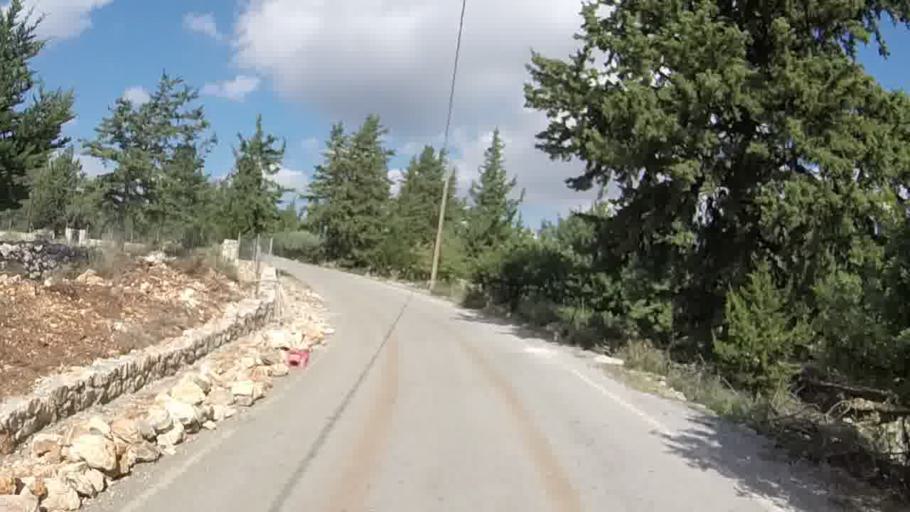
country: GR
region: Crete
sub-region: Nomos Chanias
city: Kalivai
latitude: 35.3908
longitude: 24.1274
